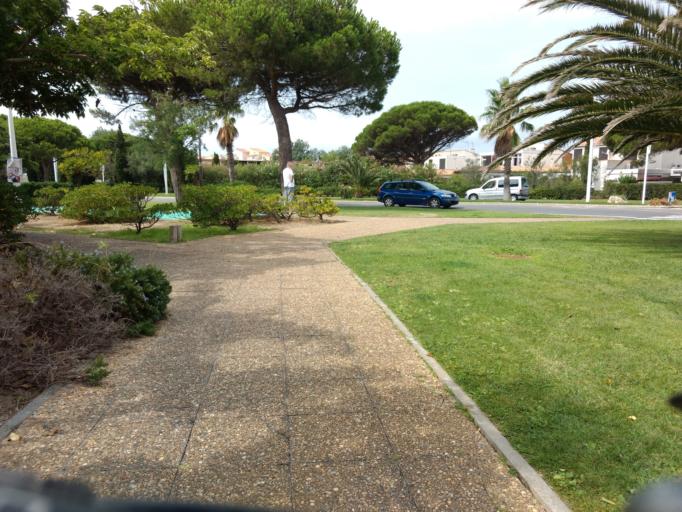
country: FR
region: Languedoc-Roussillon
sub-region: Departement de l'Aude
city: Leucate
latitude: 42.8605
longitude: 3.0415
